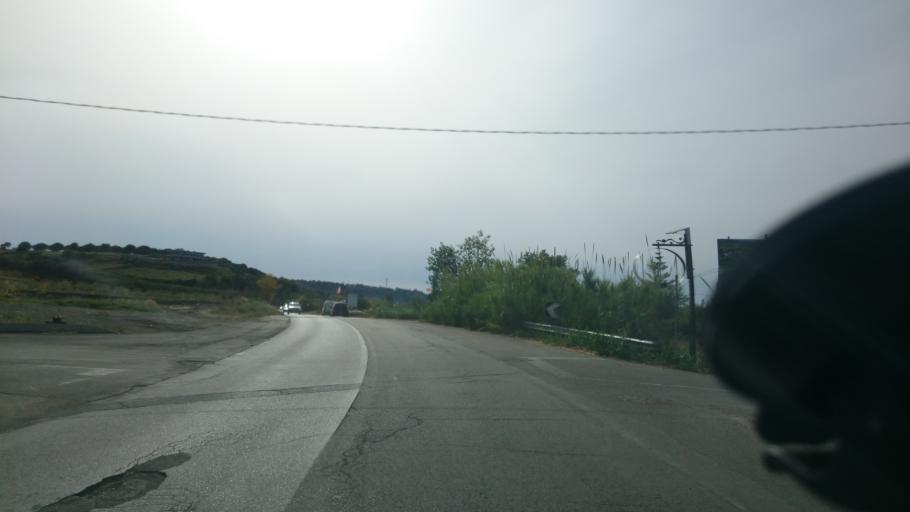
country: IT
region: Calabria
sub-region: Provincia di Vibo-Valentia
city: Pannaconi
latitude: 38.7155
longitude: 16.0609
